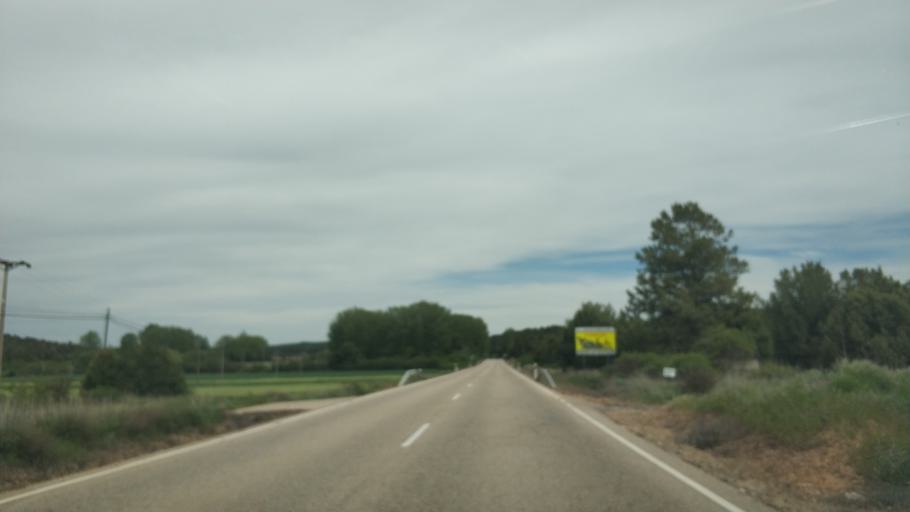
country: ES
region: Castille and Leon
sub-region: Provincia de Soria
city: Valdenebro
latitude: 41.5666
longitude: -2.9998
